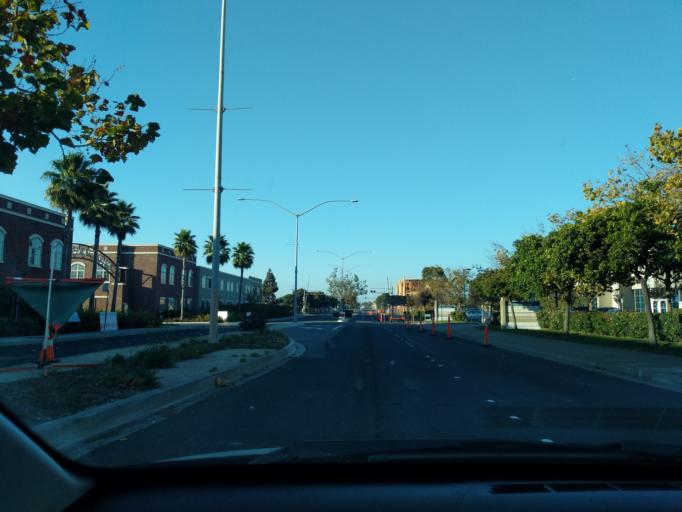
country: US
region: California
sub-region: Contra Costa County
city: Richmond
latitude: 37.9183
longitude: -122.3558
